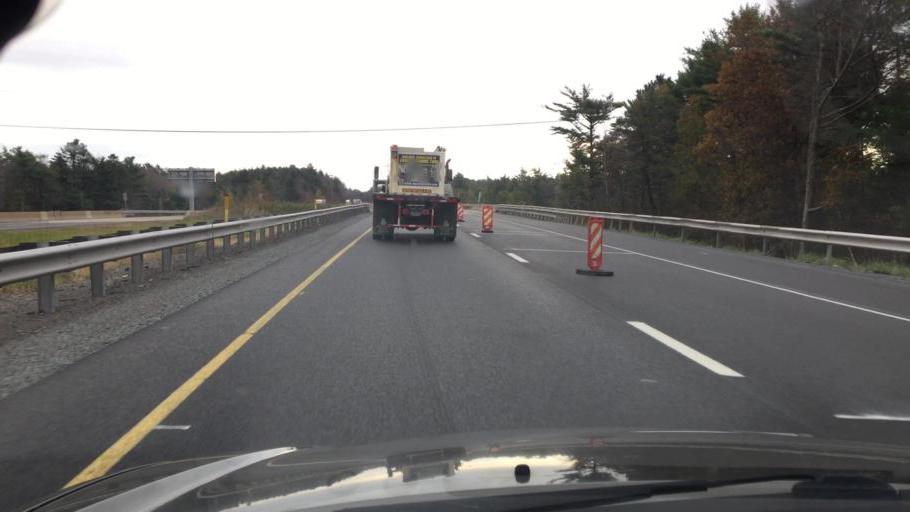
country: US
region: Pennsylvania
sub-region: Monroe County
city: Pocono Pines
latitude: 41.0769
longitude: -75.5071
